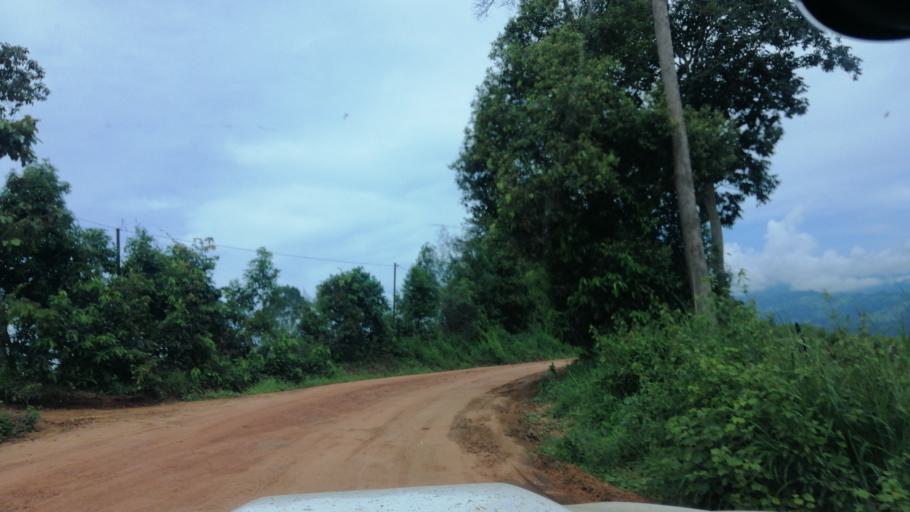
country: TH
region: Loei
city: Na Haeo
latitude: 17.5949
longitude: 101.1273
